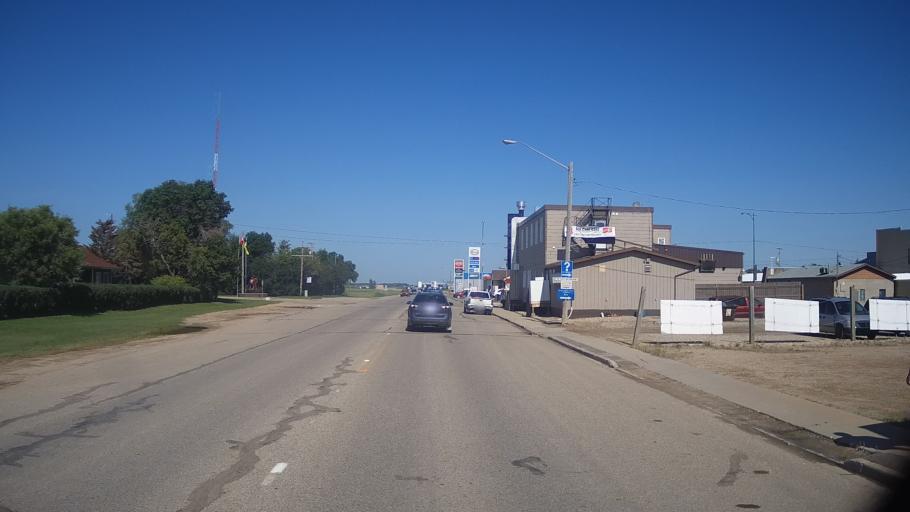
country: CA
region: Saskatchewan
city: Watrous
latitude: 51.6716
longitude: -105.4678
